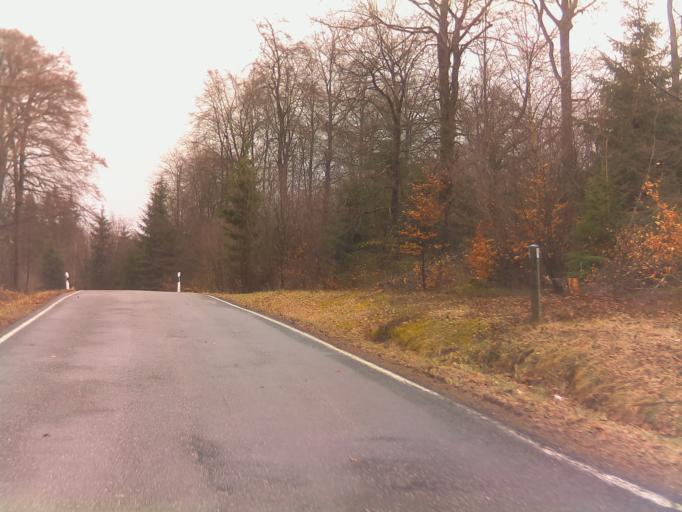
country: DE
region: Rheinland-Pfalz
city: Ippenschied
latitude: 49.9061
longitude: 7.6009
